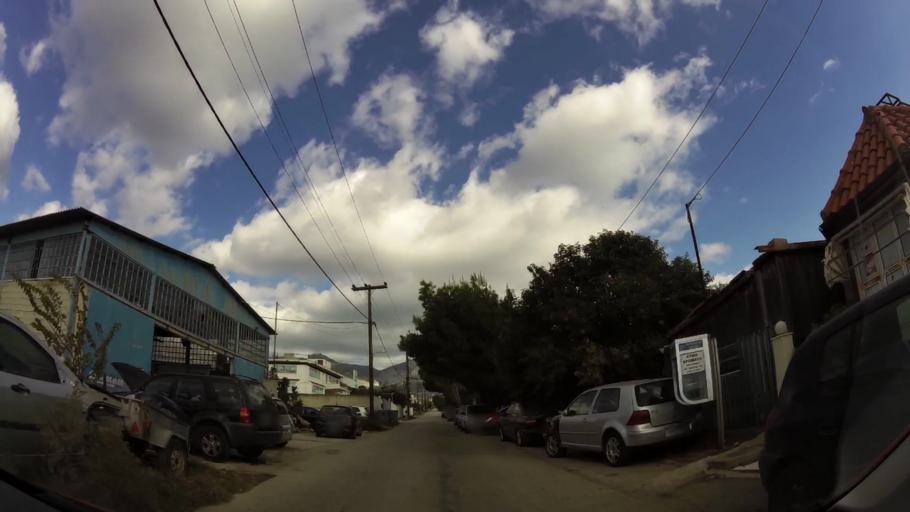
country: GR
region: Attica
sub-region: Nomarchia Anatolikis Attikis
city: Thrakomakedones
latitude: 38.1095
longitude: 23.7573
